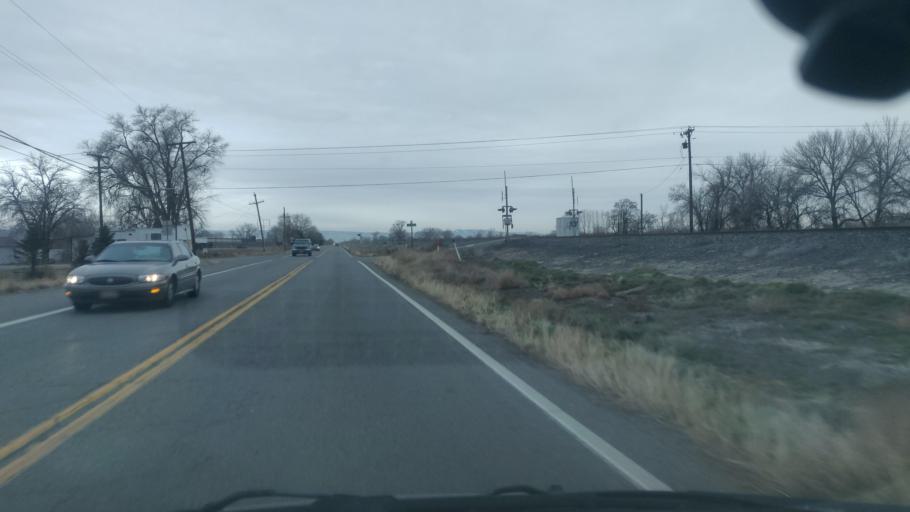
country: US
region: Colorado
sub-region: Mesa County
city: Clifton
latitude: 39.0988
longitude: -108.4031
